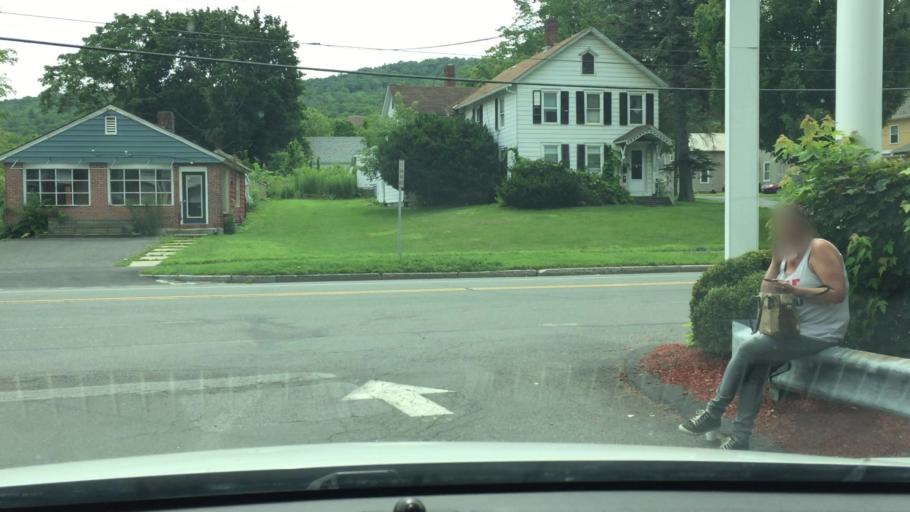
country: US
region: Massachusetts
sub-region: Berkshire County
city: Dalton
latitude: 42.4739
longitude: -73.1610
